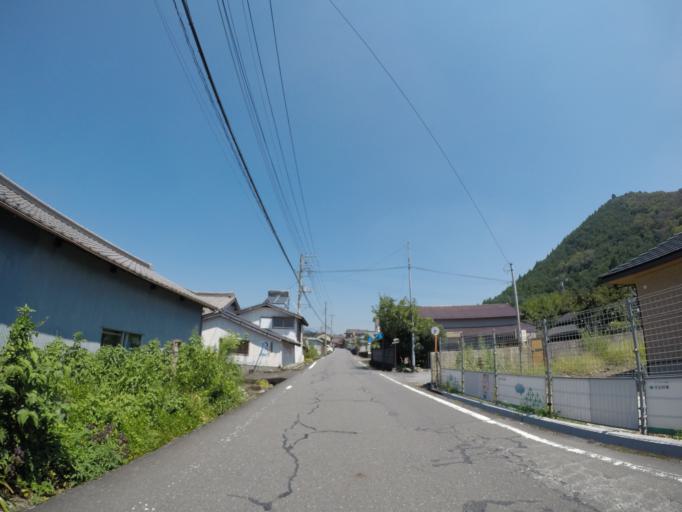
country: JP
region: Shizuoka
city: Fujinomiya
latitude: 35.2259
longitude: 138.5658
